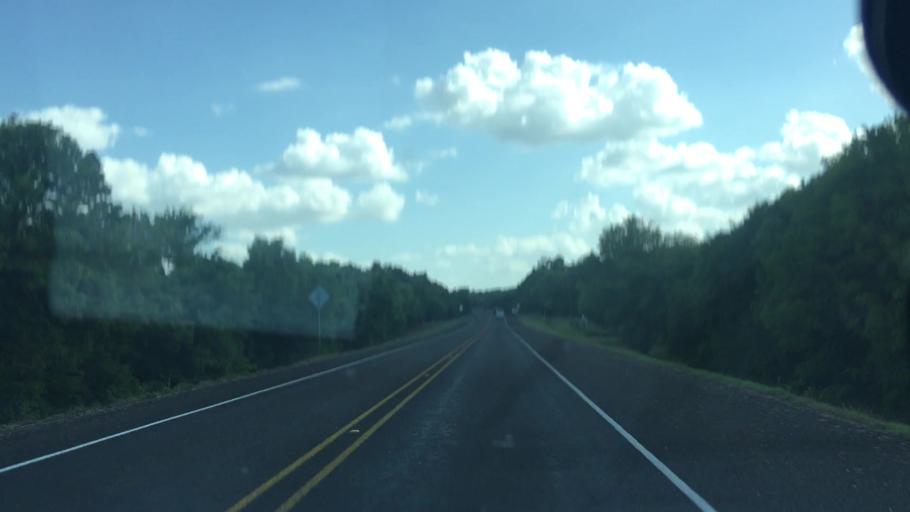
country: US
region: Texas
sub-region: Dallas County
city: Lancaster
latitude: 32.5774
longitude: -96.7572
